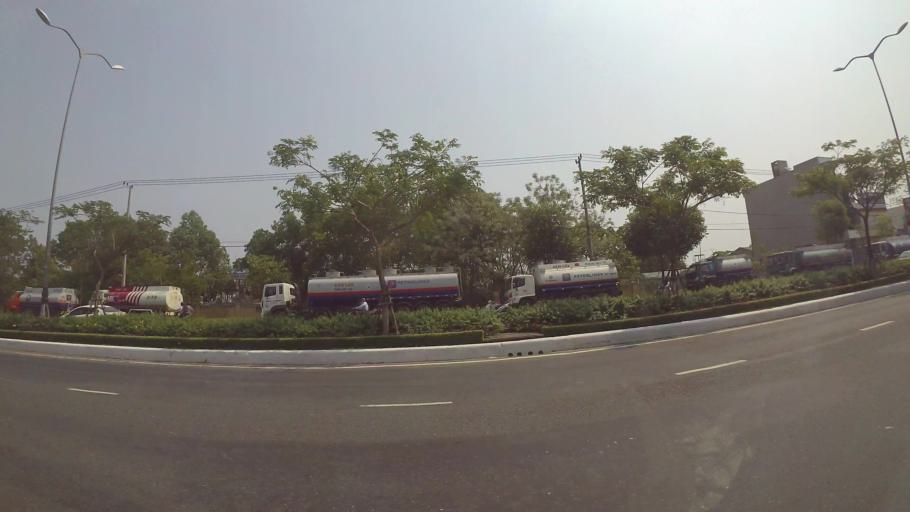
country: VN
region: Da Nang
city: Ngu Hanh Son
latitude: 16.0300
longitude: 108.2471
